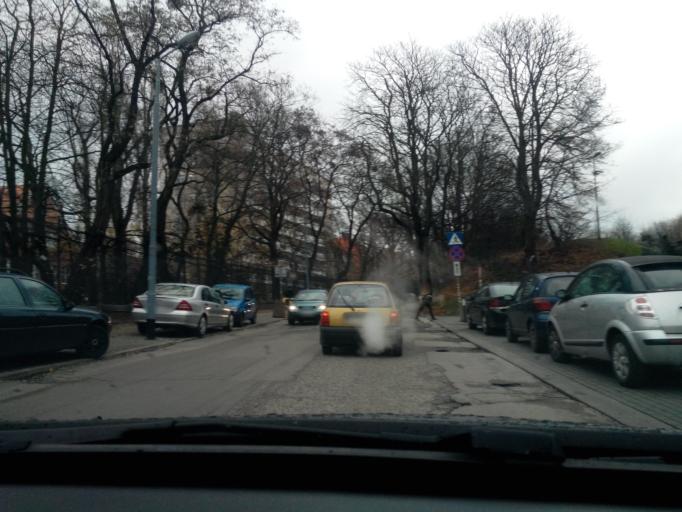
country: PL
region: Pomeranian Voivodeship
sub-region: Gdansk
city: Gdansk
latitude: 54.3704
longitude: 18.6161
